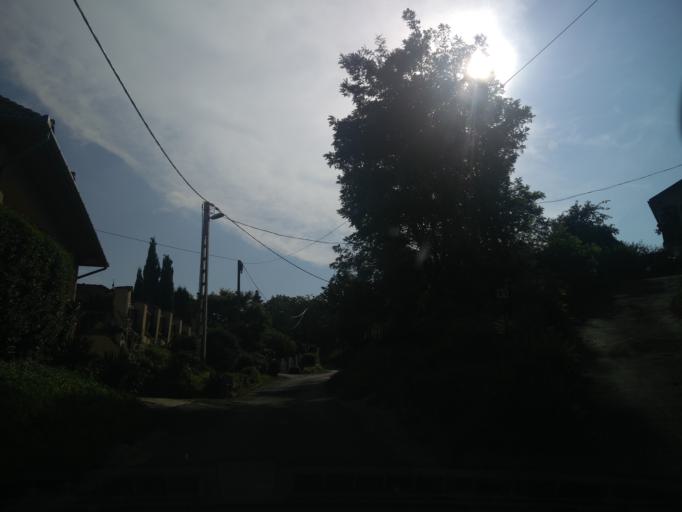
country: HU
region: Zala
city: Zalaegerszeg
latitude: 46.8429
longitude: 16.8127
